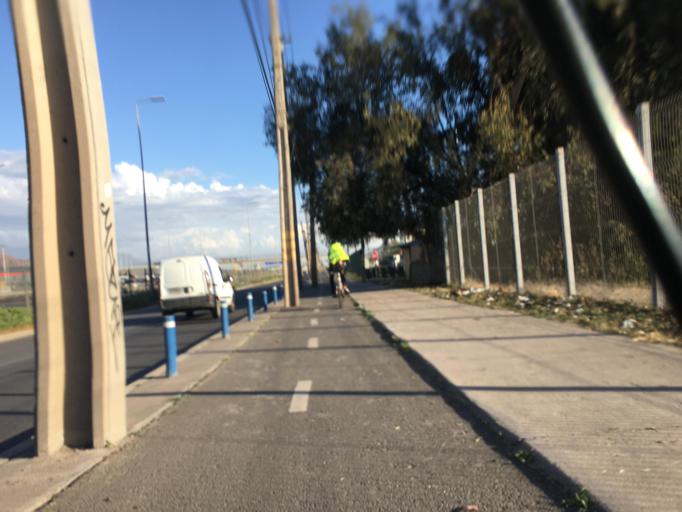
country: CL
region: Santiago Metropolitan
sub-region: Provincia de Chacabuco
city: Chicureo Abajo
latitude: -33.3186
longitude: -70.7221
